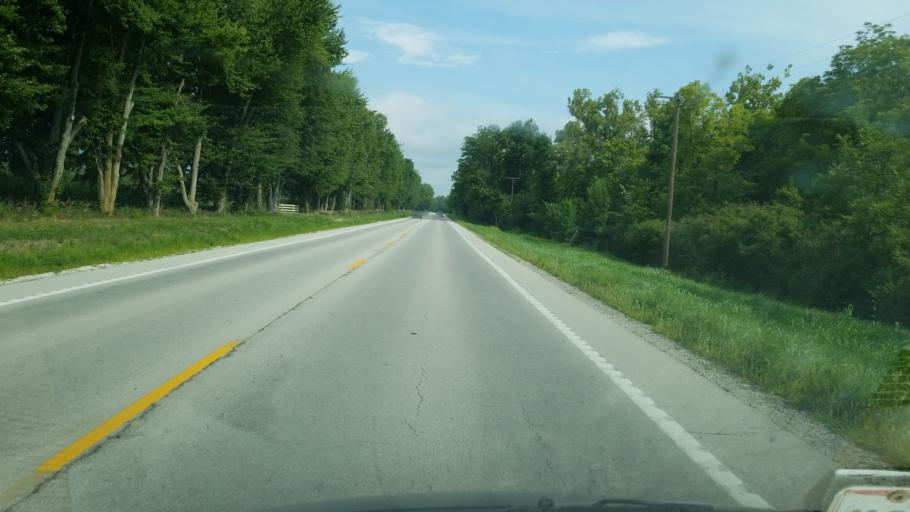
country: US
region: Ohio
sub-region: Sandusky County
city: Ballville
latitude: 41.2711
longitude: -83.1685
